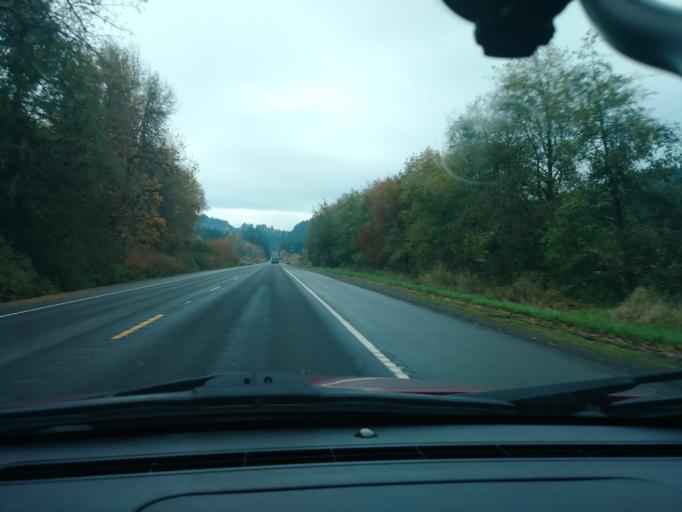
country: US
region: Oregon
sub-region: Washington County
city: Banks
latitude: 45.6148
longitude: -123.1781
